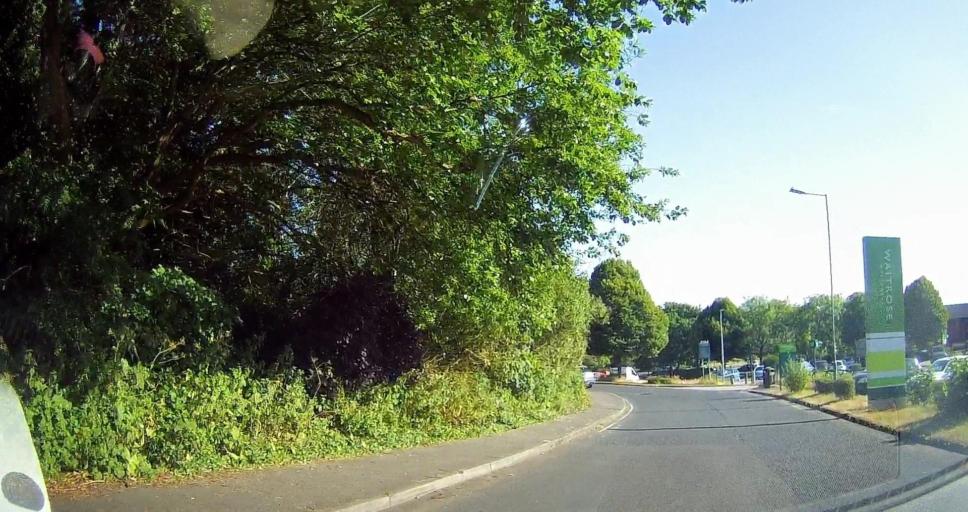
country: GB
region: England
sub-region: Cheshire East
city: Sandbach
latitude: 53.1425
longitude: -2.3621
